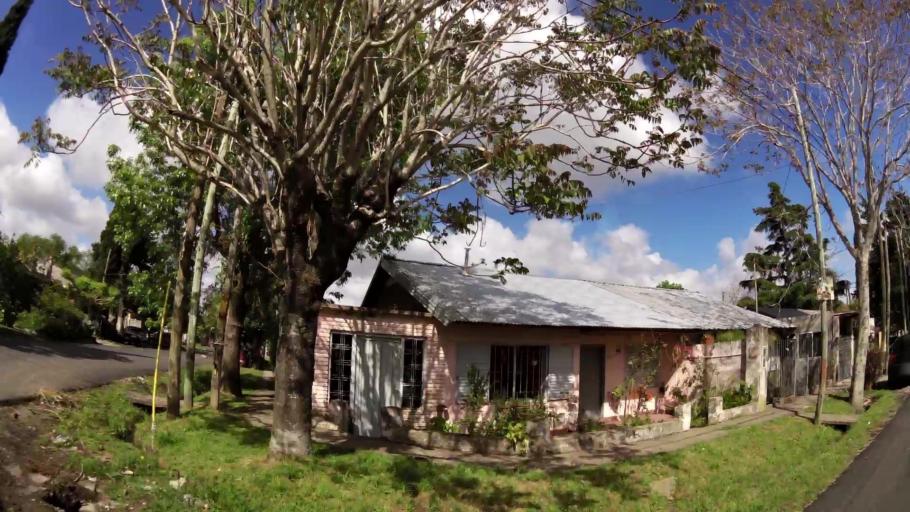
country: AR
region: Buenos Aires
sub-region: Partido de Quilmes
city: Quilmes
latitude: -34.7952
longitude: -58.1548
